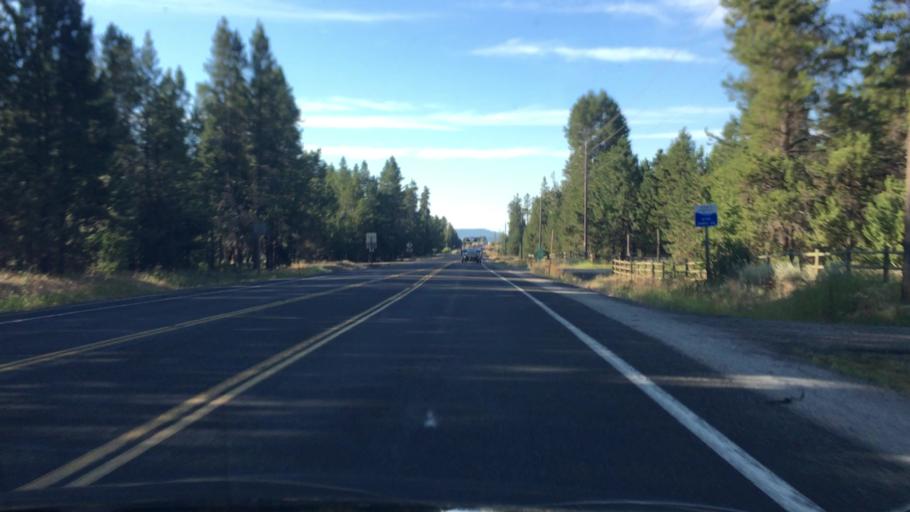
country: US
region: Idaho
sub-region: Valley County
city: Cascade
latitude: 44.4079
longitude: -115.9997
